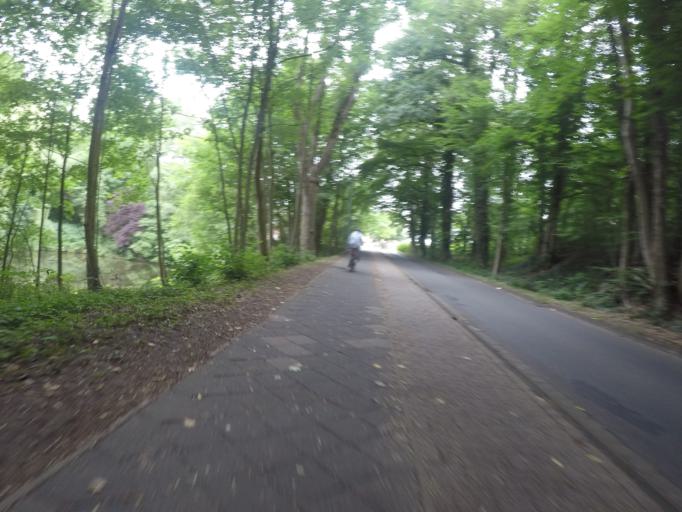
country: DE
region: Lower Saxony
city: Stade
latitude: 53.5990
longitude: 9.4496
